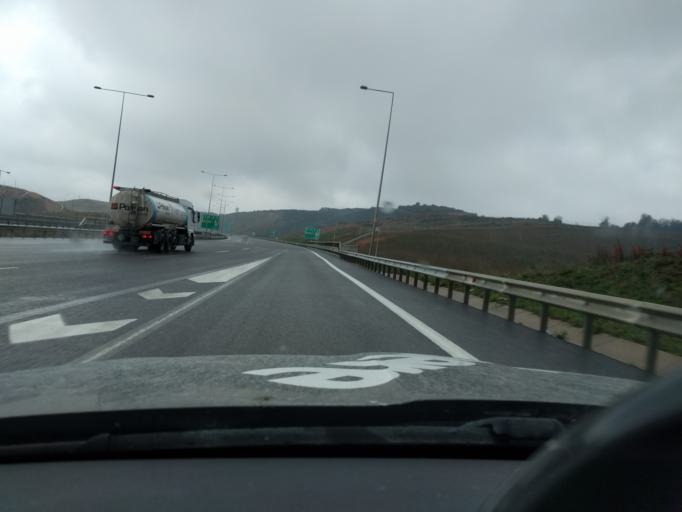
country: TR
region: Istanbul
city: Kemerburgaz
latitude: 41.2122
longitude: 28.8270
